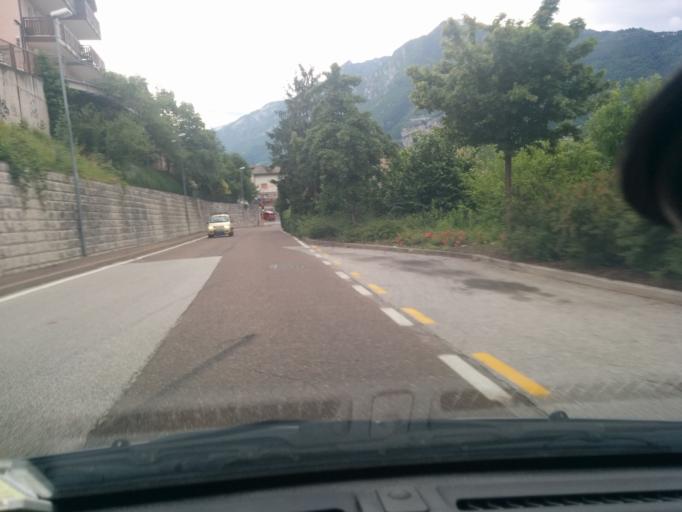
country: IT
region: Trentino-Alto Adige
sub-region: Provincia di Trento
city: Trento
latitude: 46.0871
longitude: 11.1297
